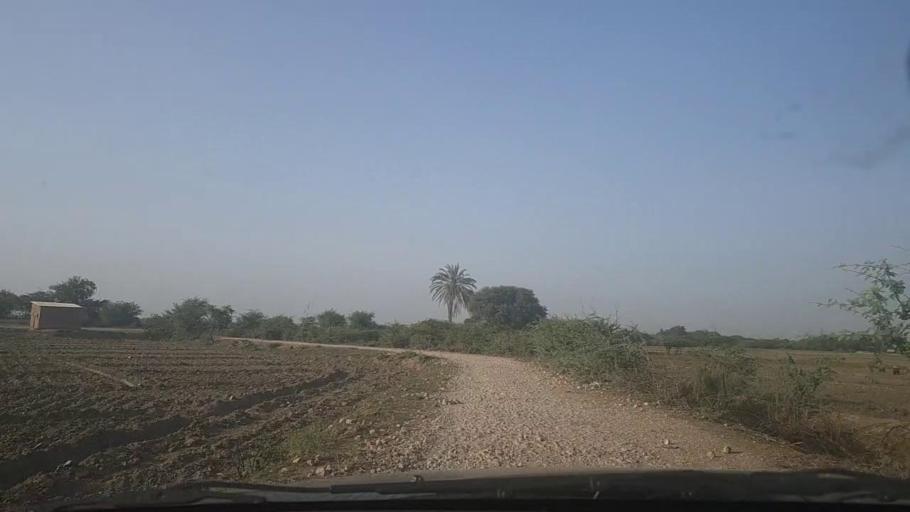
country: PK
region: Sindh
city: Keti Bandar
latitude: 24.2770
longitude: 67.5958
